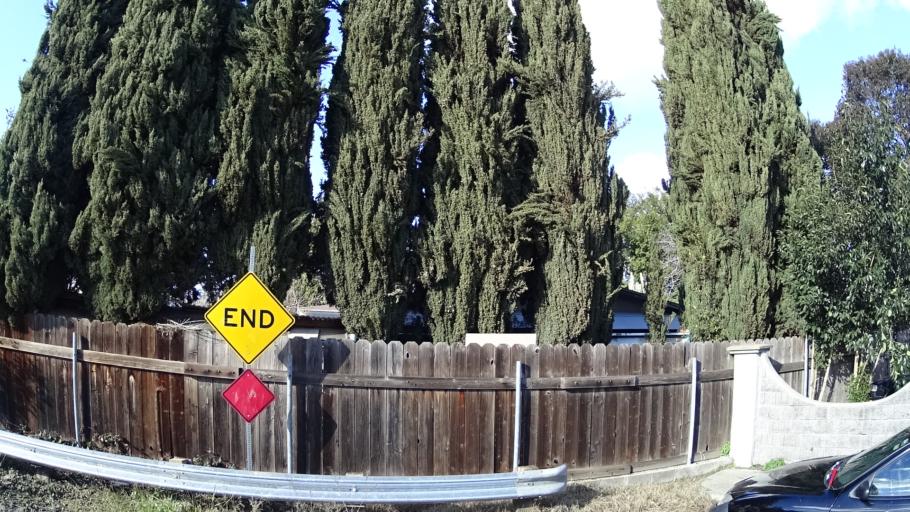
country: US
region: California
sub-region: Alameda County
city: Cherryland
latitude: 37.6783
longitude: -122.0960
